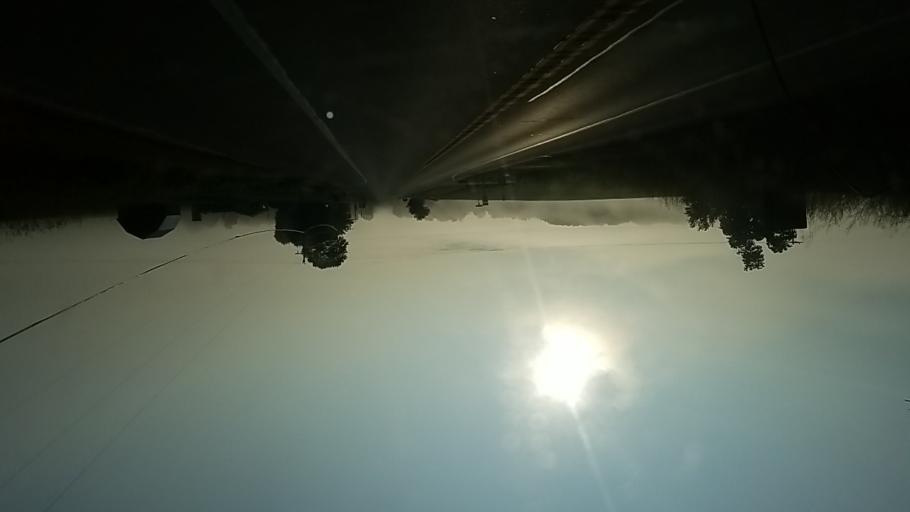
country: US
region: Michigan
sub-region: Newaygo County
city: Fremont
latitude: 43.4673
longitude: -86.0009
